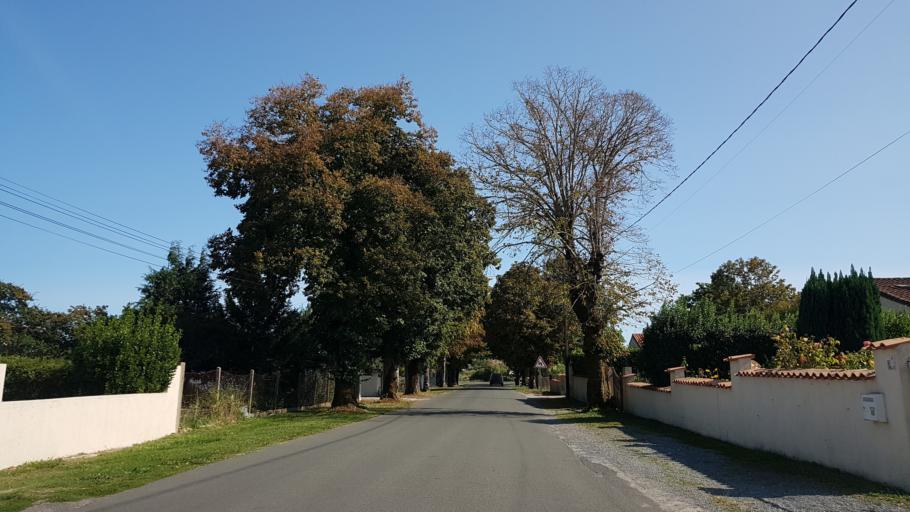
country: FR
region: Poitou-Charentes
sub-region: Departement de la Charente-Maritime
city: Breuillet
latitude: 45.7066
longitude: -1.0259
